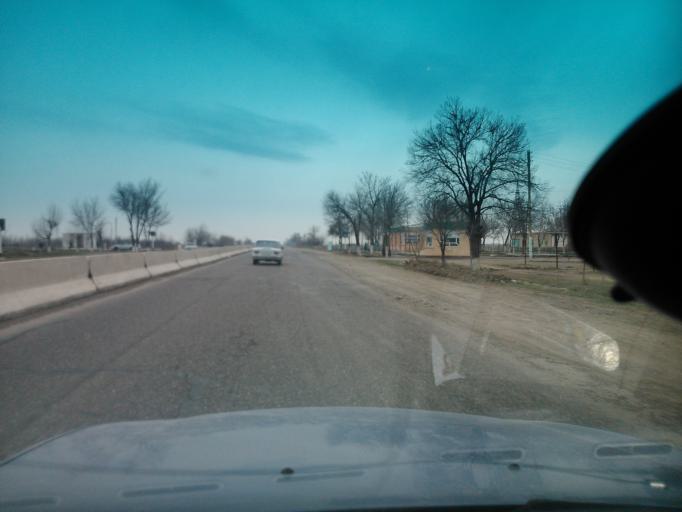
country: UZ
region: Sirdaryo
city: Guliston
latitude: 40.4113
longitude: 68.7873
